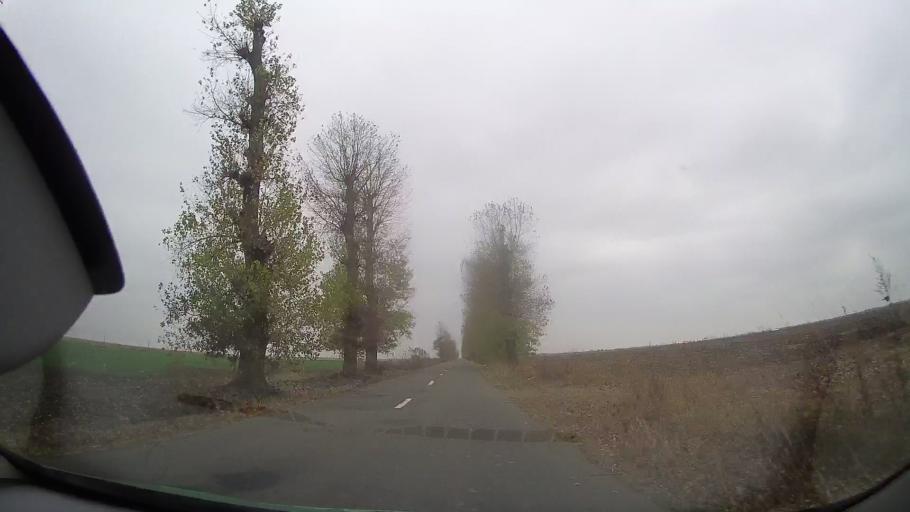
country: RO
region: Ialomita
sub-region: Comuna Valea Macrisului
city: Valea Macrisului
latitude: 44.7534
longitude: 26.8727
